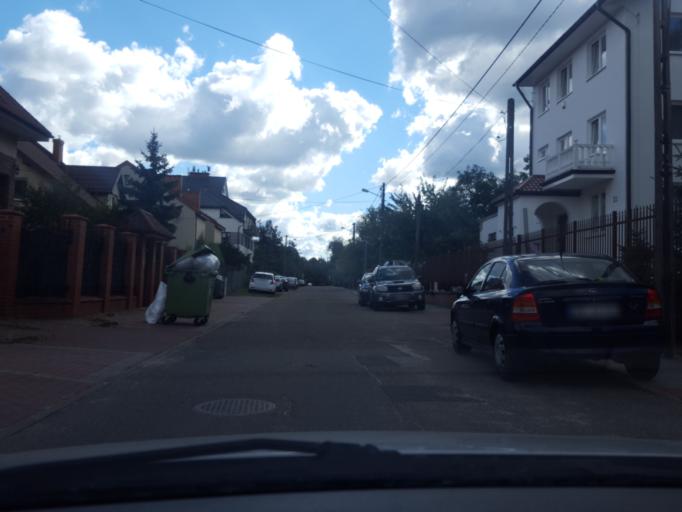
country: PL
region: Masovian Voivodeship
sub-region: Warszawa
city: Rembertow
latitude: 52.2699
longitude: 21.1669
